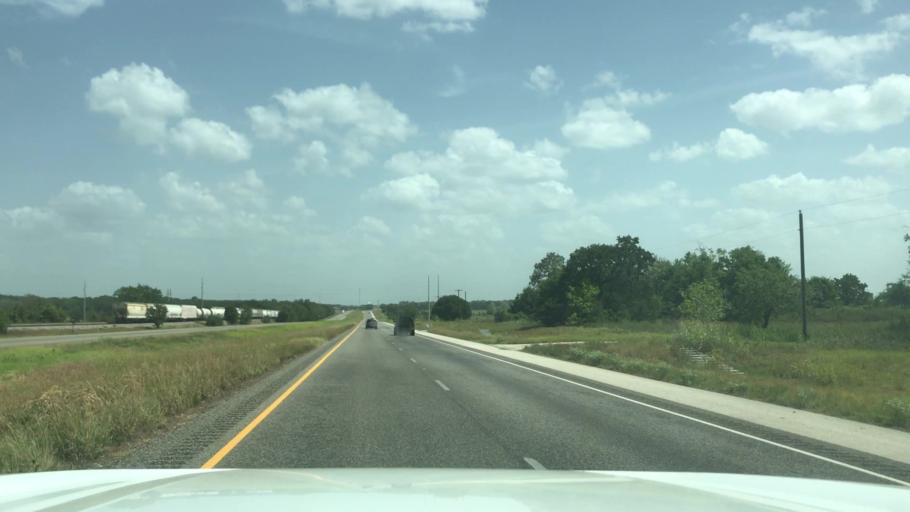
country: US
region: Texas
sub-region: Robertson County
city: Hearne
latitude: 30.9208
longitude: -96.6231
